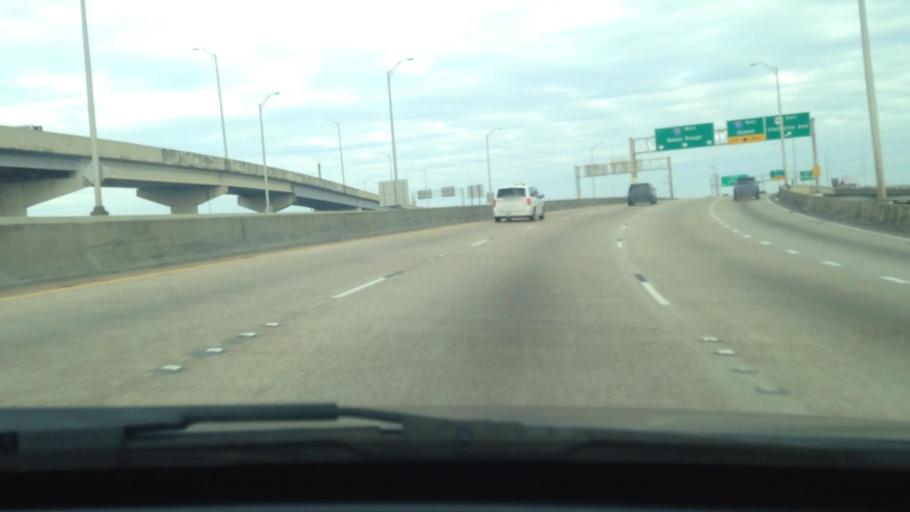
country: US
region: Louisiana
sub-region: Orleans Parish
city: New Orleans
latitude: 29.9488
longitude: -90.0841
